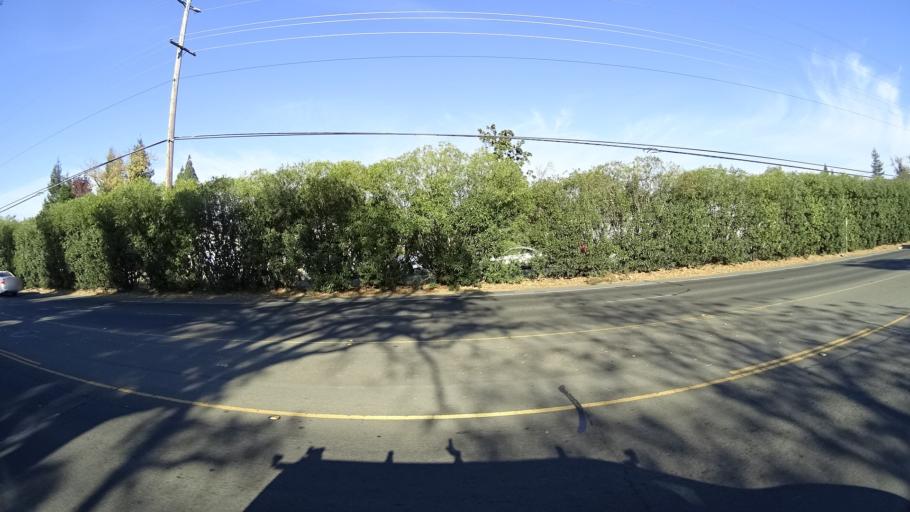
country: US
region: California
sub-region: Sacramento County
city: Citrus Heights
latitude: 38.6912
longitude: -121.3002
